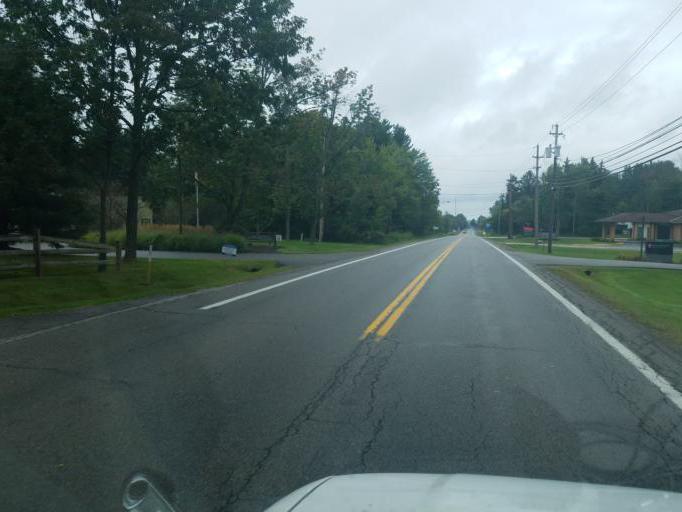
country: US
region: Ohio
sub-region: Geauga County
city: Burton
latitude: 41.5077
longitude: -81.1936
